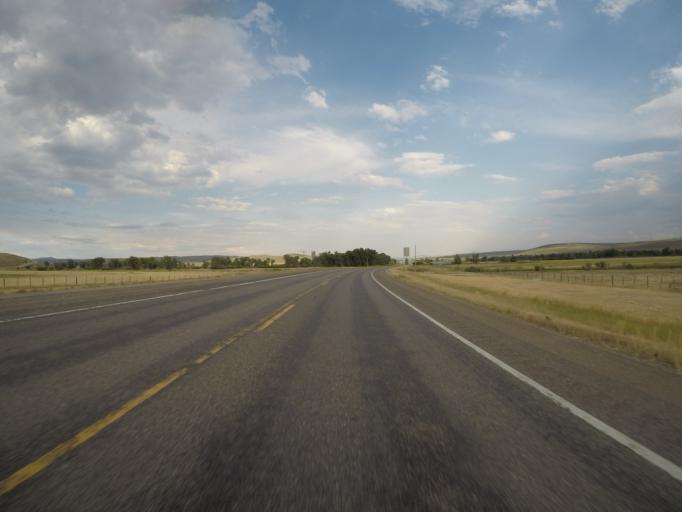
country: US
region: Colorado
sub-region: Moffat County
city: Craig
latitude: 40.5332
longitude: -107.4396
